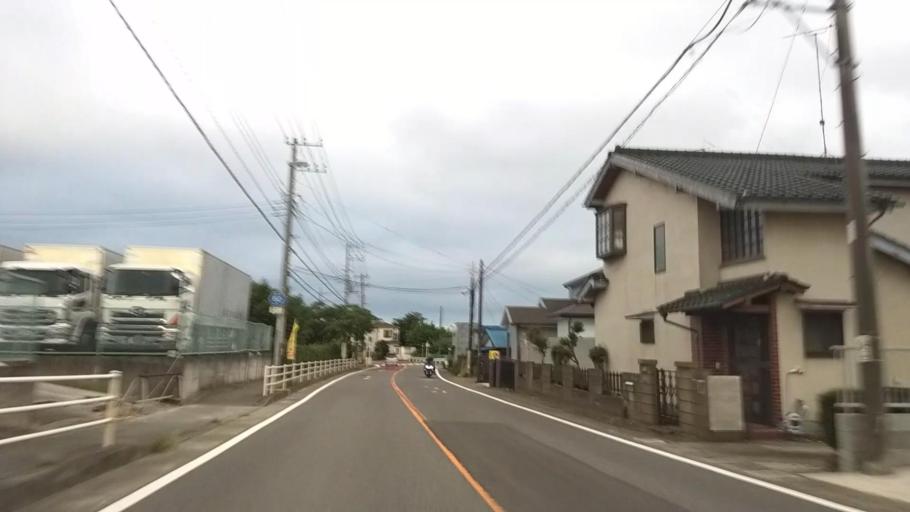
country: JP
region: Kanagawa
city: Atsugi
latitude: 35.4681
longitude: 139.3326
